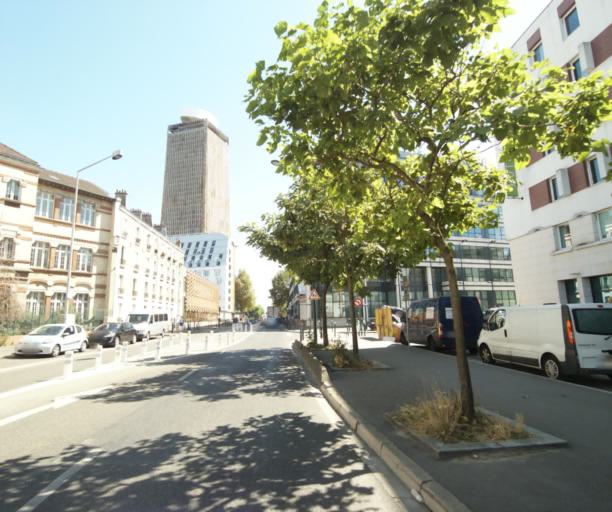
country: FR
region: Ile-de-France
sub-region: Paris
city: Saint-Ouen
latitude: 48.9221
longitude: 2.3435
